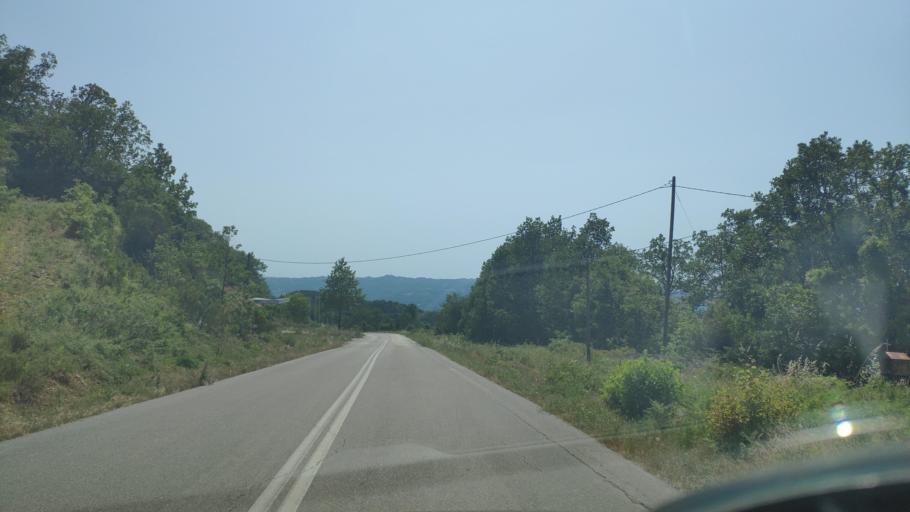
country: GR
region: Epirus
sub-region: Nomos Artas
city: Ano Kalentini
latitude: 39.2511
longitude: 21.1888
